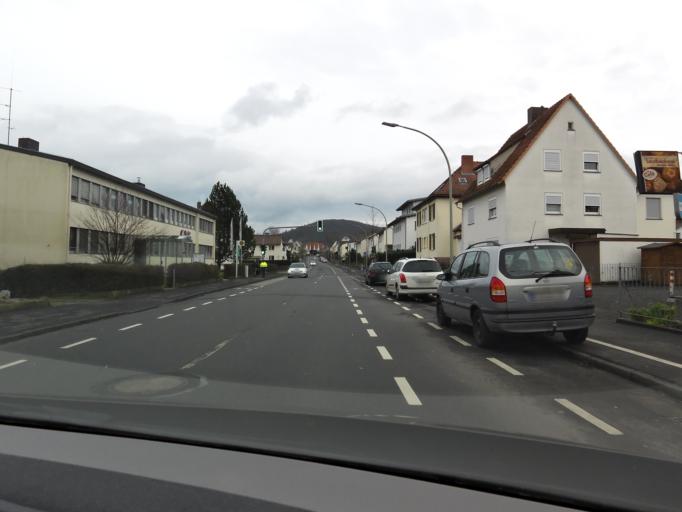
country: DE
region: Hesse
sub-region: Regierungsbezirk Kassel
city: Eschwege
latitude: 51.1816
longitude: 10.0596
